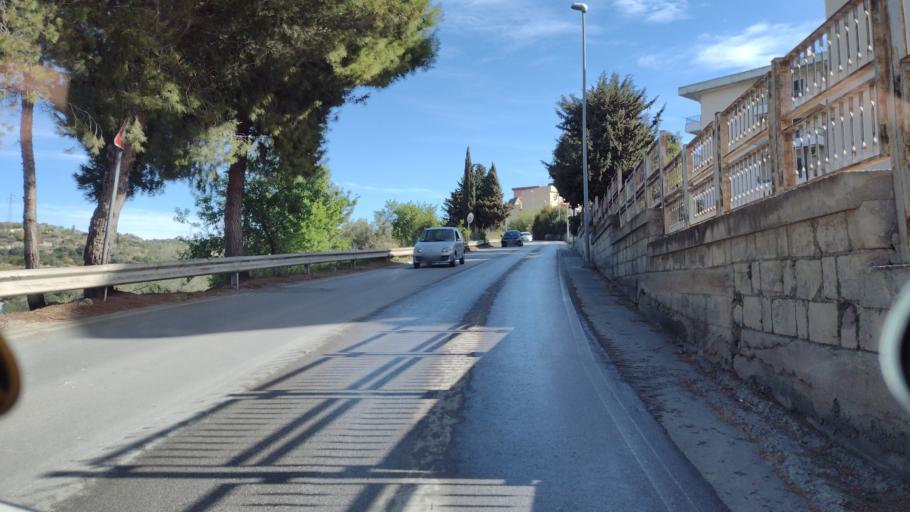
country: IT
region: Sicily
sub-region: Provincia di Siracusa
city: Noto
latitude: 36.8959
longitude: 15.0623
